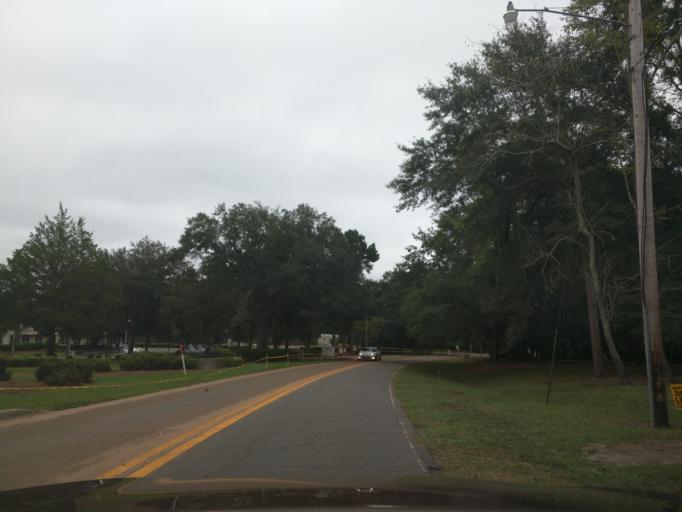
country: US
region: Florida
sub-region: Leon County
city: Tallahassee
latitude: 30.4604
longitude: -84.2425
